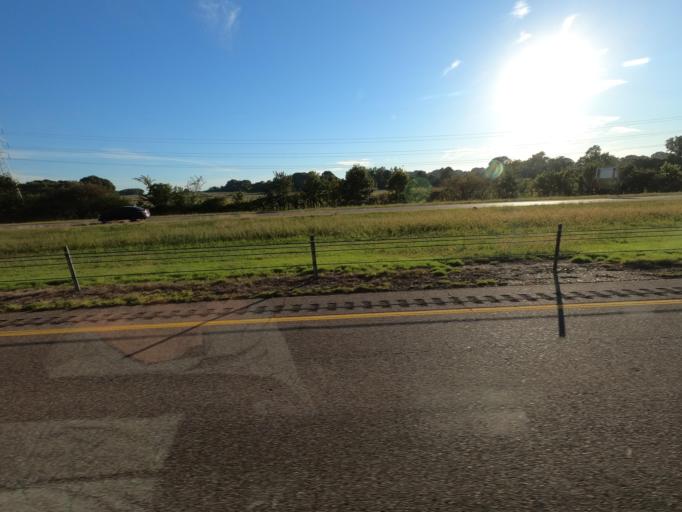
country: US
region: Tennessee
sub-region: Shelby County
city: Millington
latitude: 35.3151
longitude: -89.8661
